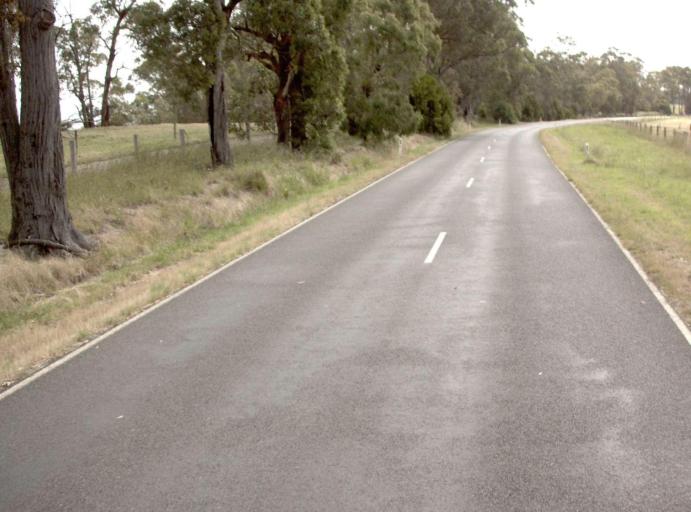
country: AU
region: Victoria
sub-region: Latrobe
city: Traralgon
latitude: -38.3791
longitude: 146.7891
